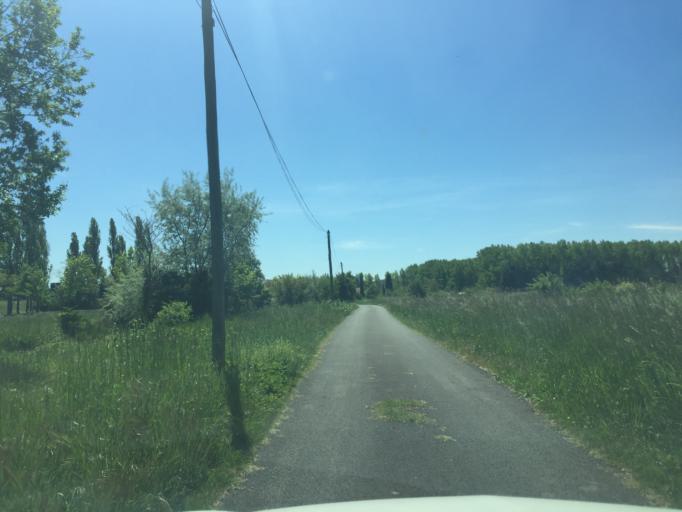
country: FR
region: Provence-Alpes-Cote d'Azur
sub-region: Departement du Vaucluse
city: Caderousse
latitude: 44.1035
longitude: 4.7881
